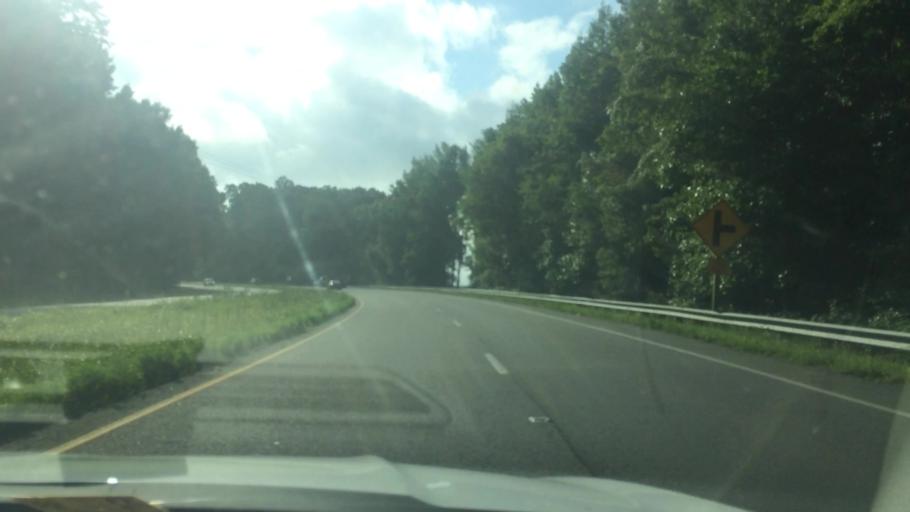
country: US
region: Virginia
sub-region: Gloucester County
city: Gloucester Courthouse
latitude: 37.4254
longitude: -76.4903
